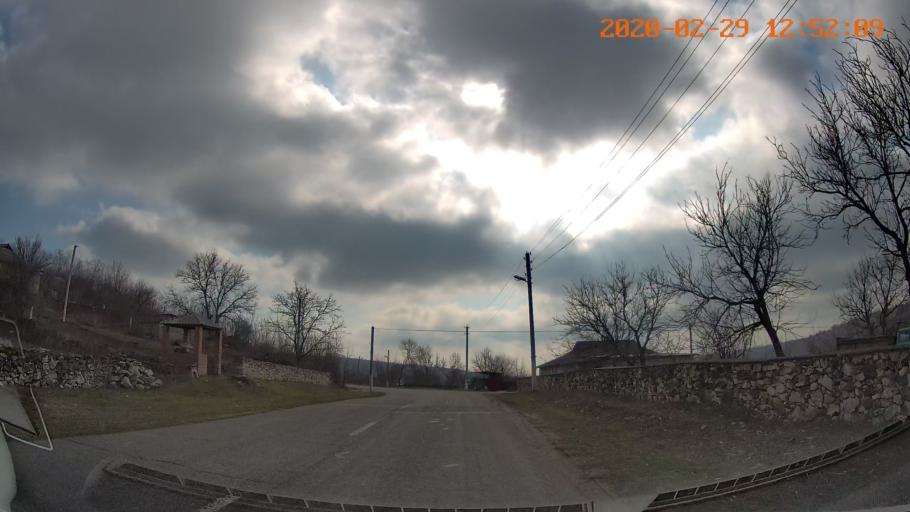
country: MD
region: Telenesti
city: Camenca
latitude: 48.1139
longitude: 28.7322
